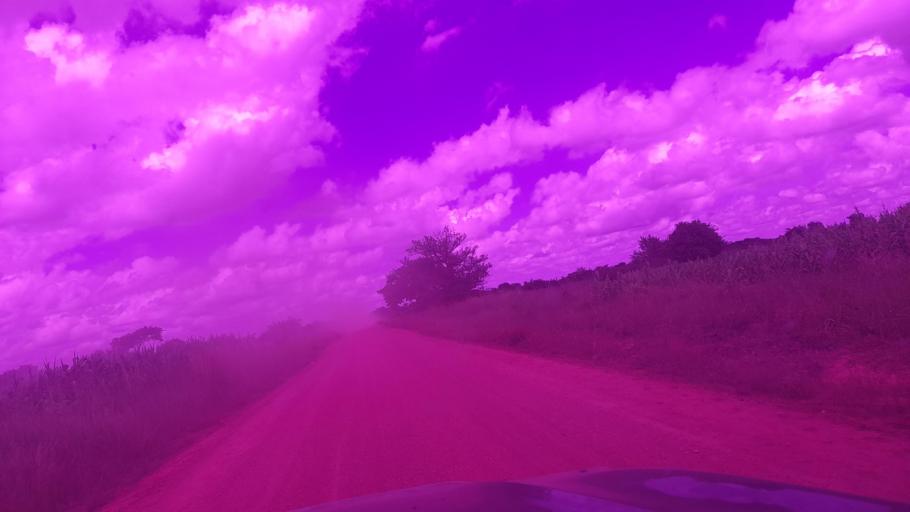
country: ZM
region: Central
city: Chibombo
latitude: -14.7116
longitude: 27.9884
